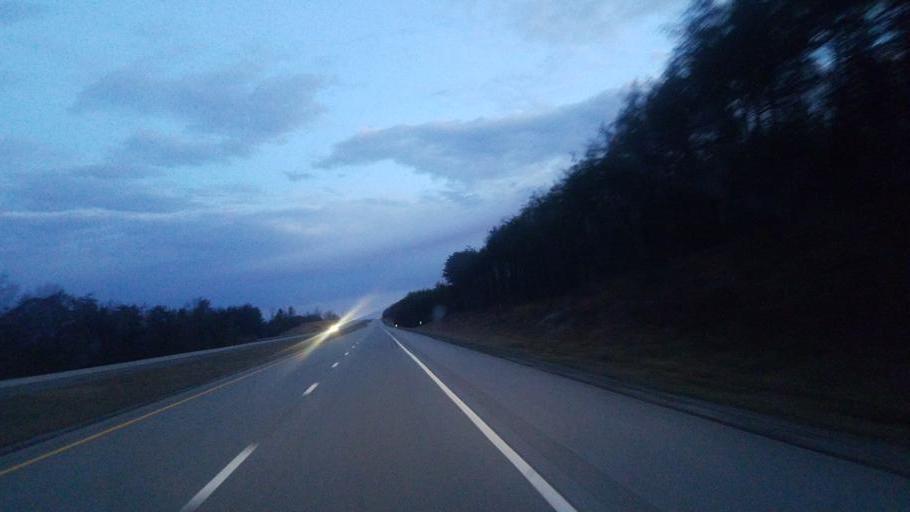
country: US
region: Tennessee
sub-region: Van Buren County
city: Spencer
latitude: 35.6469
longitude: -85.4736
